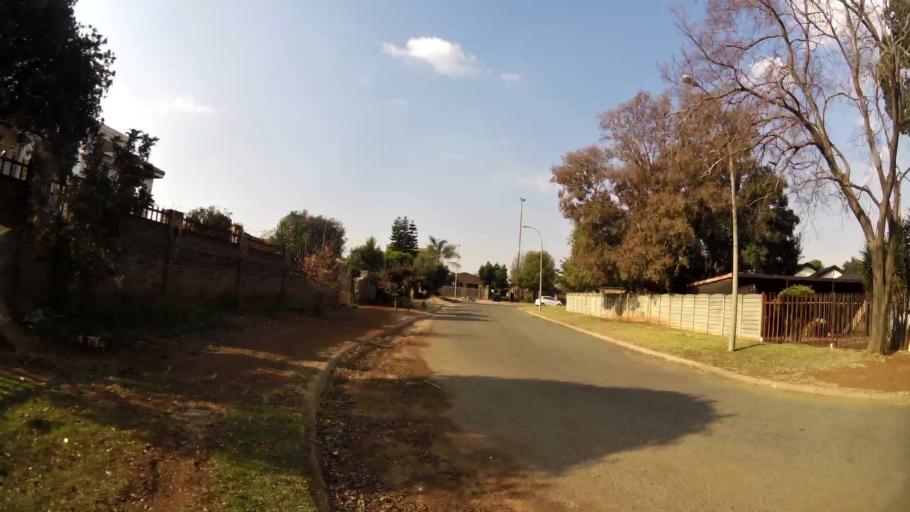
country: ZA
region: Gauteng
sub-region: City of Johannesburg Metropolitan Municipality
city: Modderfontein
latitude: -26.1015
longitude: 28.1938
